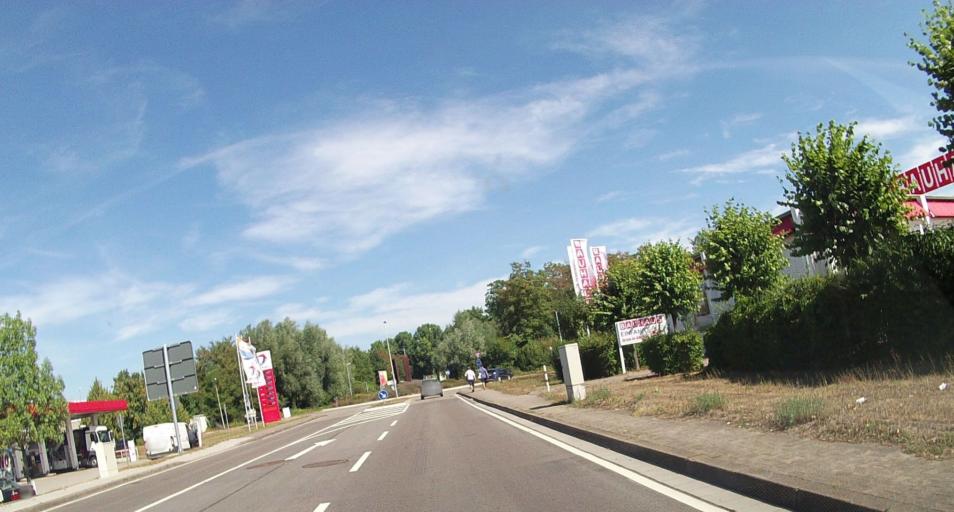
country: DE
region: Baden-Wuerttemberg
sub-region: Karlsruhe Region
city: Otigheim
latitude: 48.8610
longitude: 8.2400
